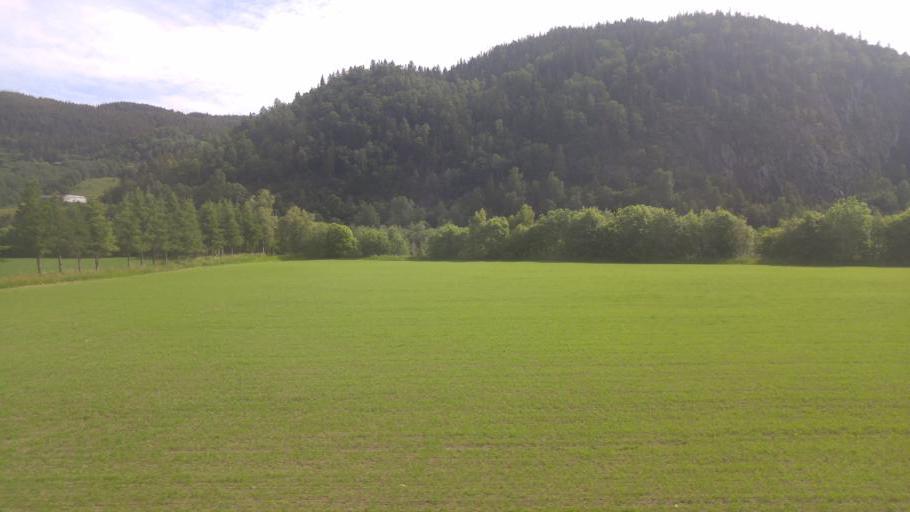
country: NO
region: Sor-Trondelag
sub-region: Midtre Gauldal
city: Storen
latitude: 63.0851
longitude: 10.2454
